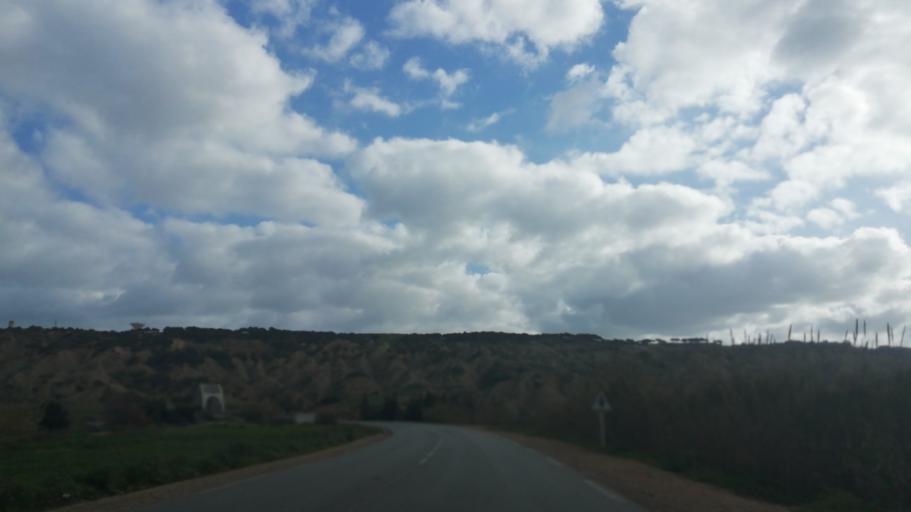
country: DZ
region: Relizane
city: Mazouna
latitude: 36.3023
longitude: 0.6674
